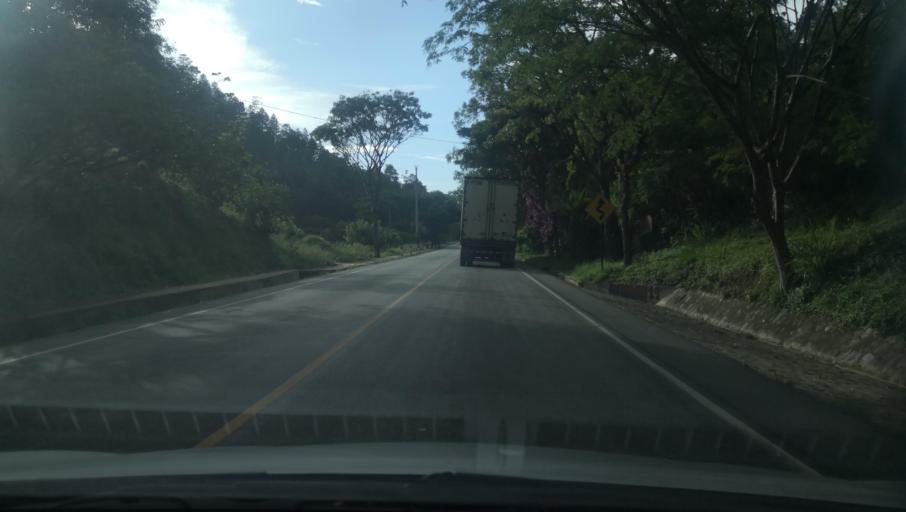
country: NI
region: Nueva Segovia
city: Mozonte
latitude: 13.7228
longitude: -86.5064
